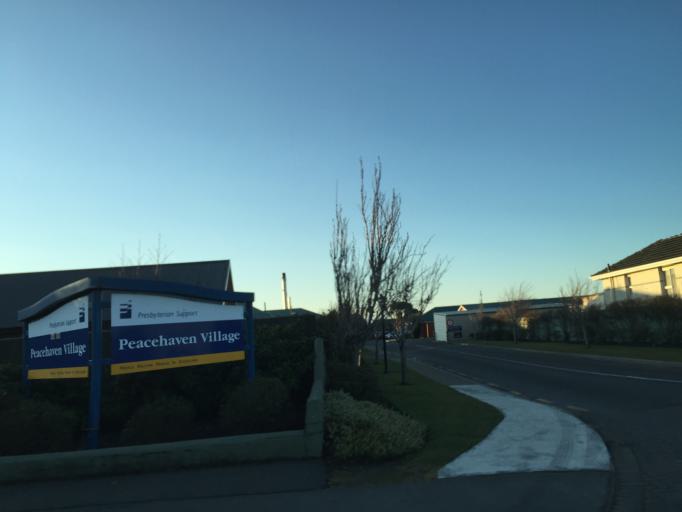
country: NZ
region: Southland
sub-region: Invercargill City
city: Invercargill
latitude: -46.4178
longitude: 168.3774
